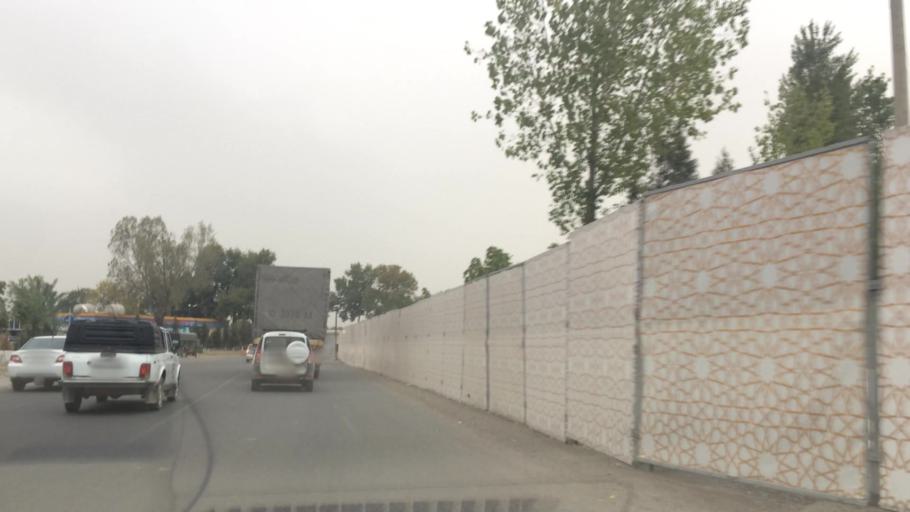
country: UZ
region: Toshkent
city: Salor
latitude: 41.3067
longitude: 69.3413
